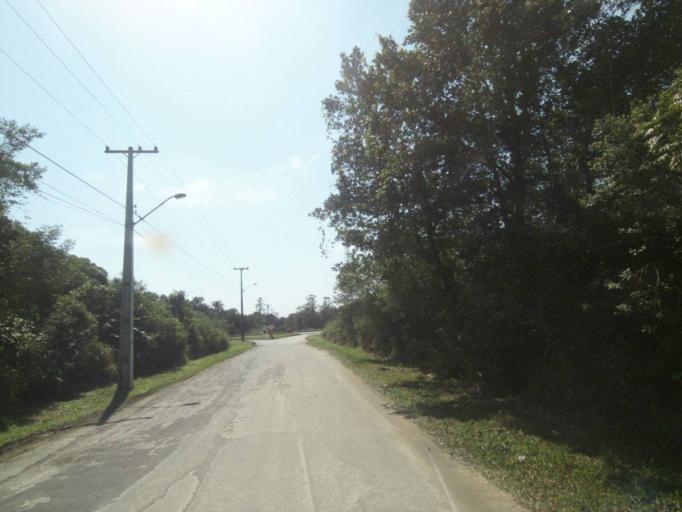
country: BR
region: Parana
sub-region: Paranagua
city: Paranagua
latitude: -25.5656
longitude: -48.6297
